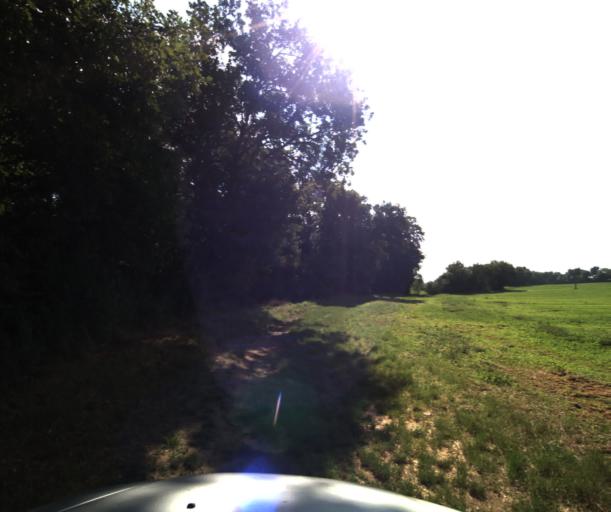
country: FR
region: Midi-Pyrenees
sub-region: Departement de la Haute-Garonne
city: Vieille-Toulouse
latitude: 43.5172
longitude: 1.4273
